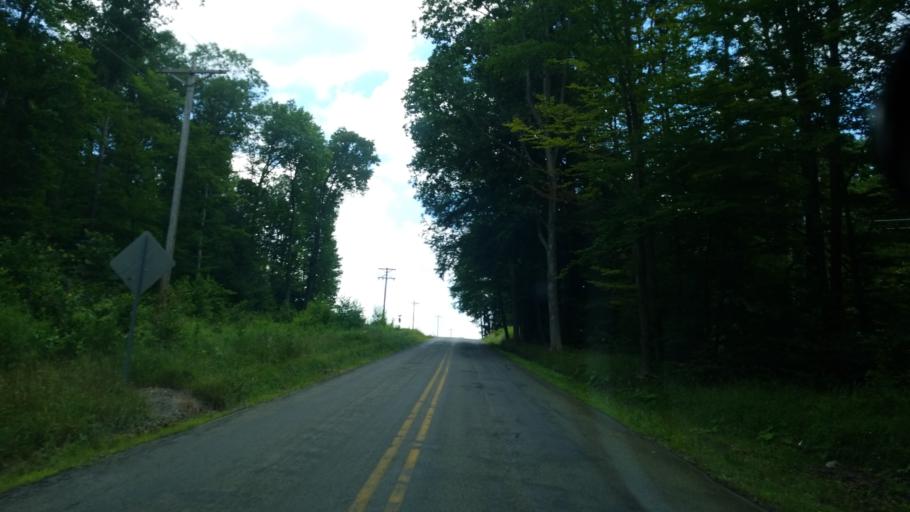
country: US
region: Pennsylvania
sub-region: Jefferson County
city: Brookville
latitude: 41.2388
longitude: -79.0407
